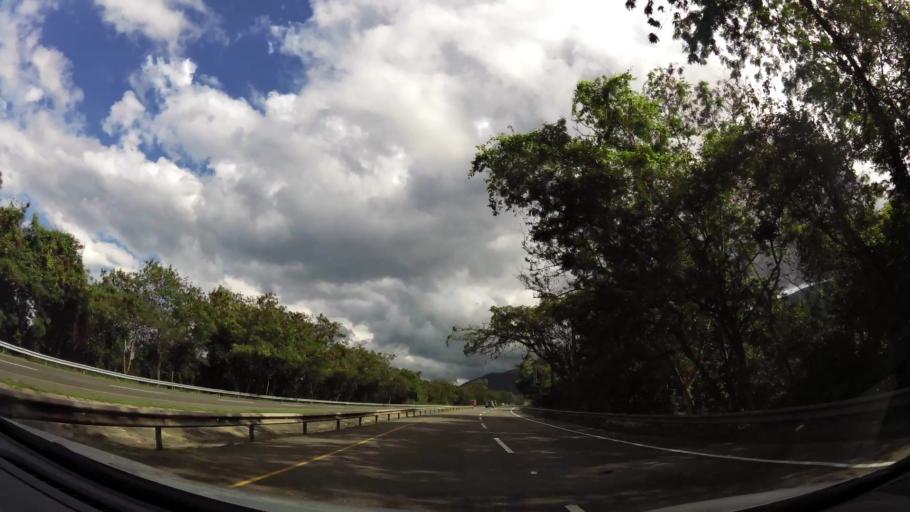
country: DO
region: La Vega
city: Concepcion de La Vega
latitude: 19.1646
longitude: -70.4860
